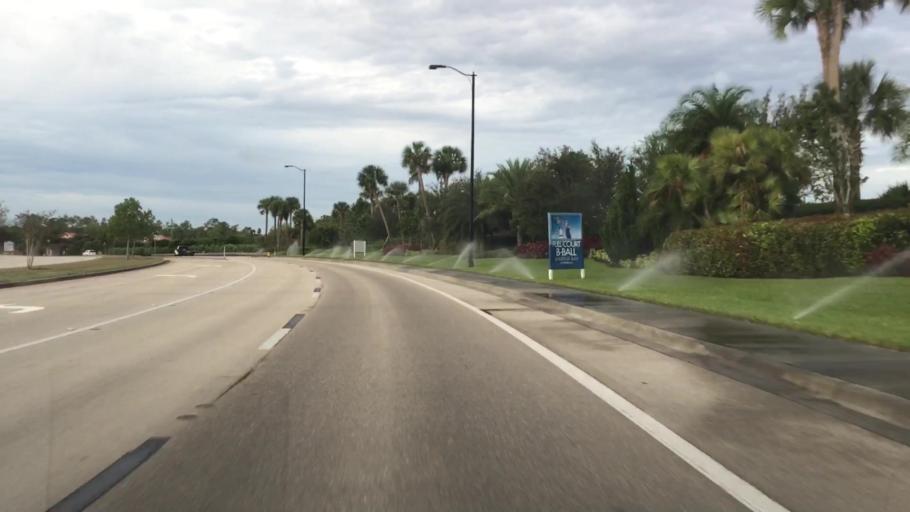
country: US
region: Florida
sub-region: Lee County
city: Gateway
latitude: 26.5672
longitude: -81.7851
